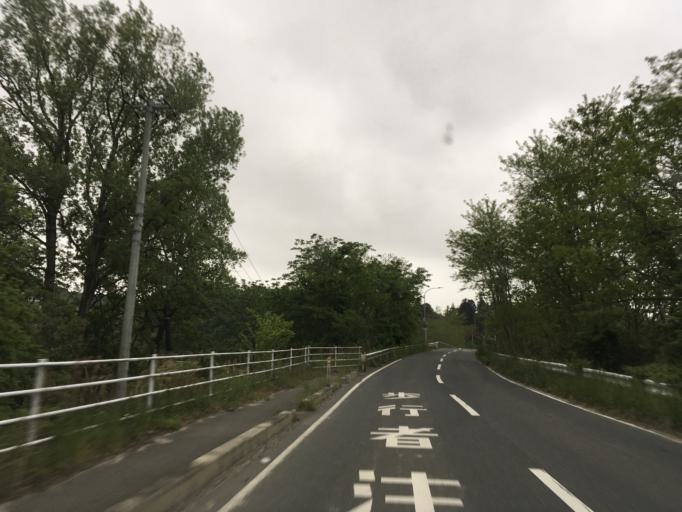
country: JP
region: Miyagi
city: Wakuya
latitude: 38.7158
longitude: 141.2954
